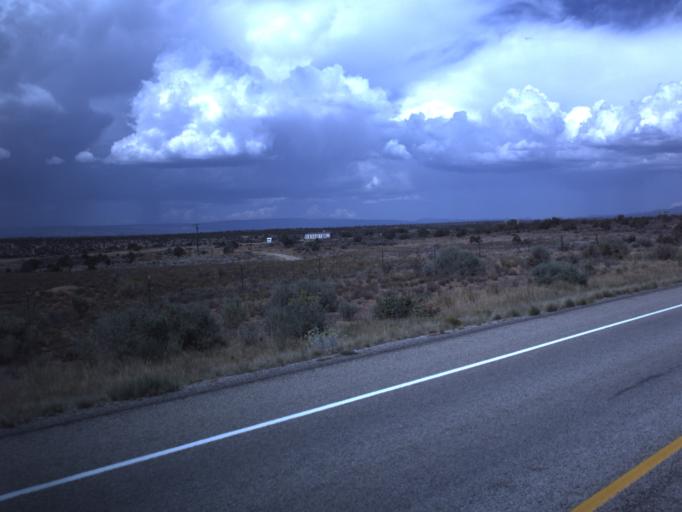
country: US
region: Utah
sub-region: San Juan County
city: Blanding
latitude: 37.4704
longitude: -109.4670
